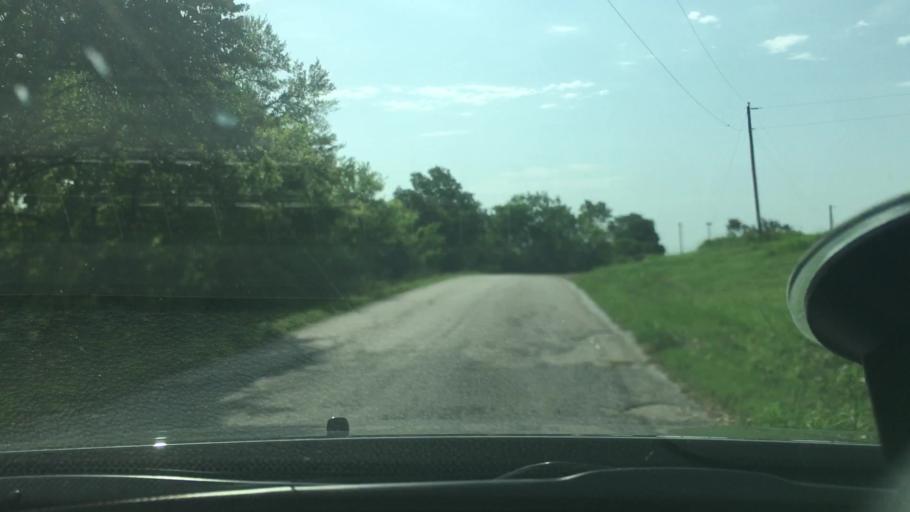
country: US
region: Oklahoma
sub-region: Atoka County
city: Atoka
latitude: 34.4687
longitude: -96.0416
